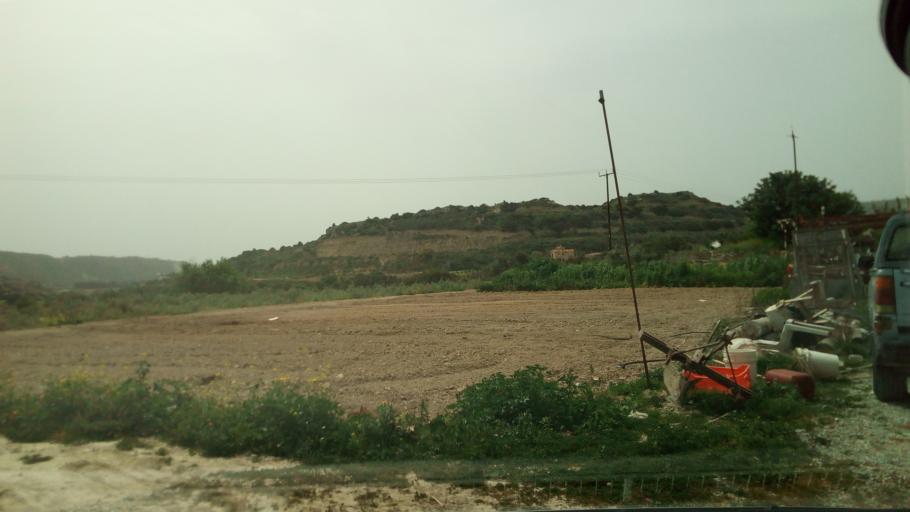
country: CY
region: Limassol
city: Pissouri
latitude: 34.6803
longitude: 32.7304
